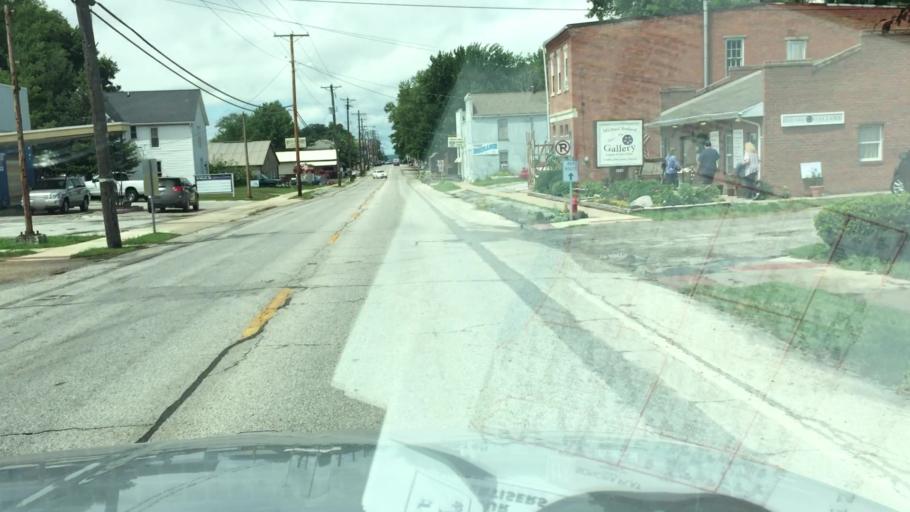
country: US
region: Illinois
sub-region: Hancock County
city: Nauvoo
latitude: 40.5497
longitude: -91.3768
